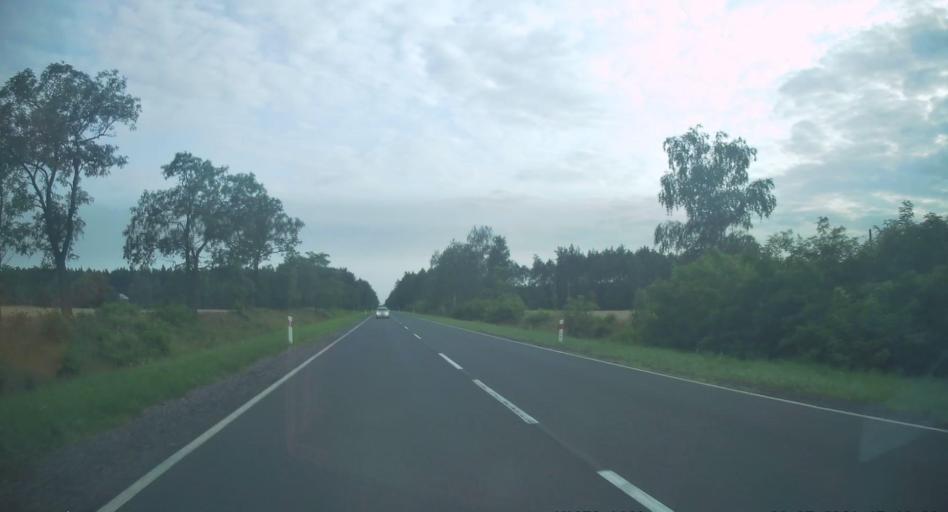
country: PL
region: Lodz Voivodeship
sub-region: Powiat radomszczanski
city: Plawno
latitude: 50.9898
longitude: 19.4141
